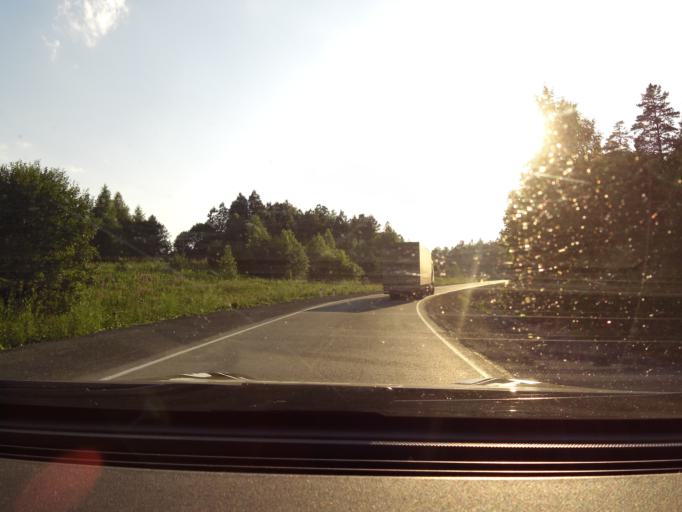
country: RU
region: Sverdlovsk
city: Druzhinino
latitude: 56.8003
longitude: 59.4686
